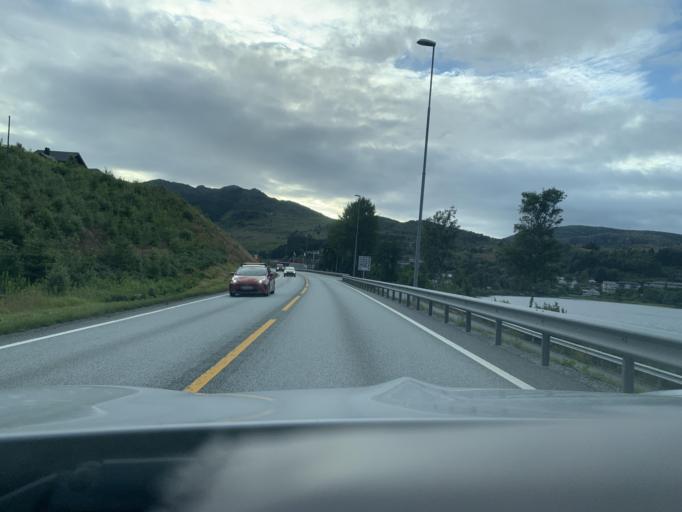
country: NO
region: Rogaland
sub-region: Bjerkreim
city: Vikesa
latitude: 58.6284
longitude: 6.0870
